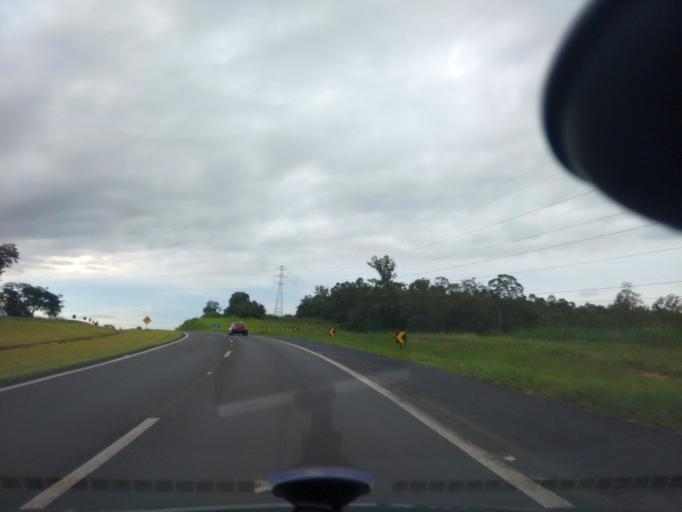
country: BR
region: Sao Paulo
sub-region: Rio Claro
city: Rio Claro
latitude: -22.3135
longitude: -47.6627
